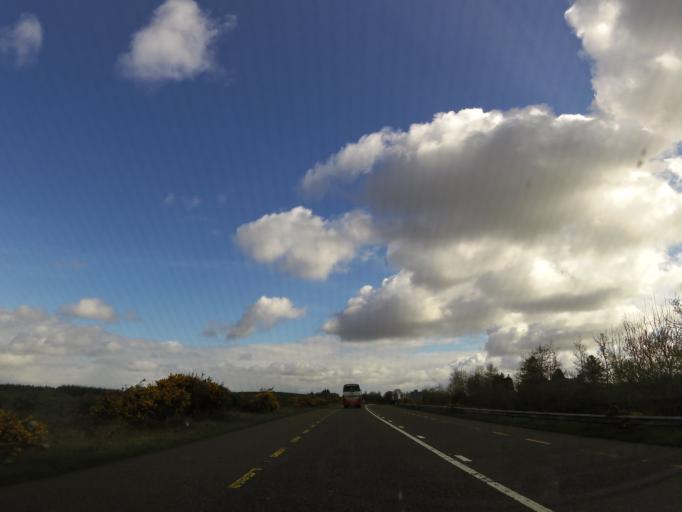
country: IE
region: Connaught
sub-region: Maigh Eo
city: Kiltamagh
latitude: 53.8188
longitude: -8.8931
